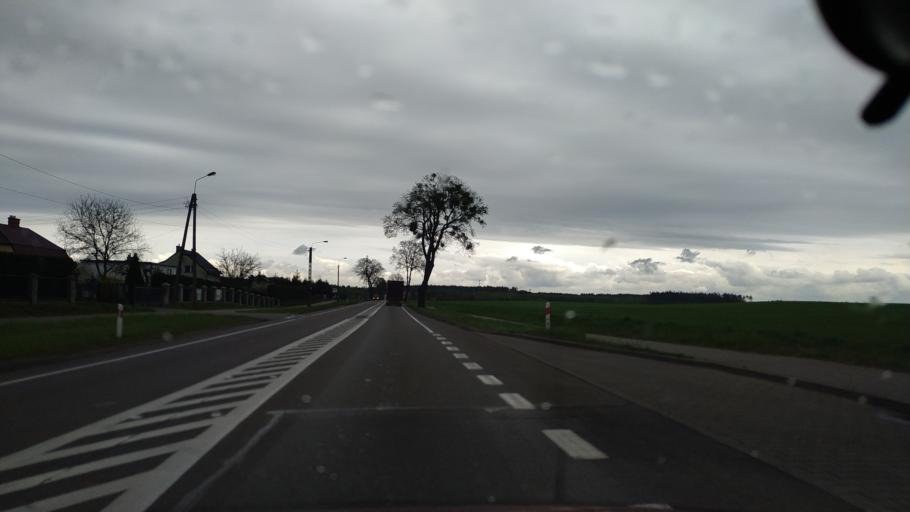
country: PL
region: Pomeranian Voivodeship
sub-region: Powiat starogardzki
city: Kaliska
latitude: 53.8883
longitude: 18.2171
